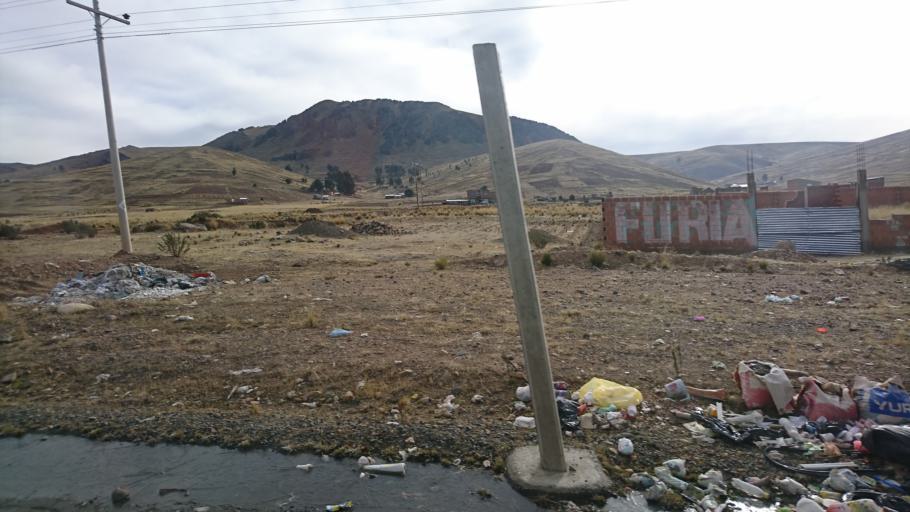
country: BO
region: La Paz
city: La Paz
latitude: -16.4178
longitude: -68.3416
